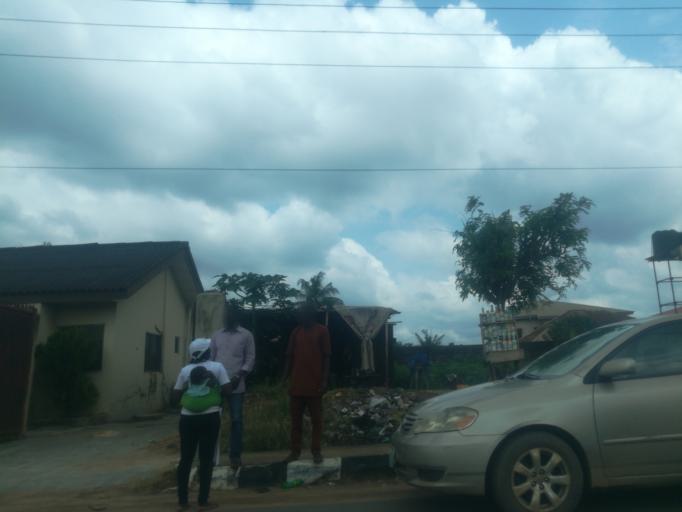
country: NG
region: Oyo
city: Ibadan
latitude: 7.3644
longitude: 3.8447
